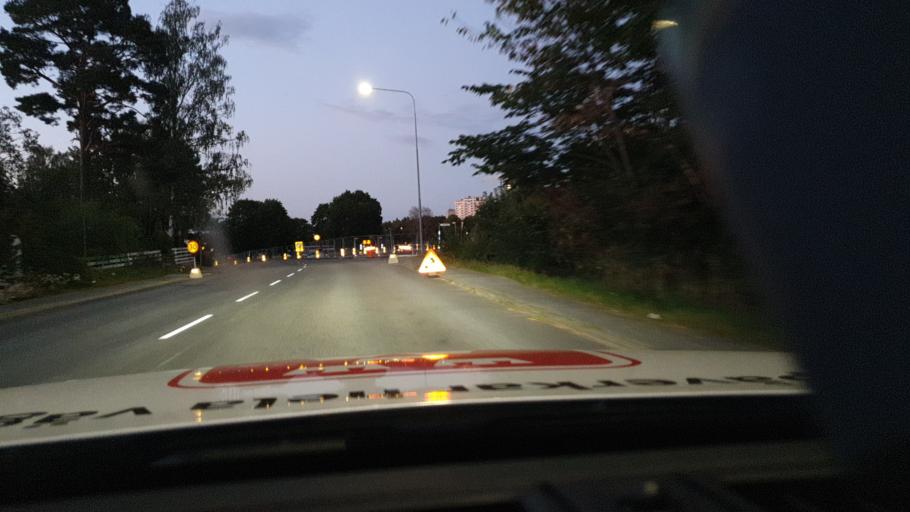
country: SE
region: Stockholm
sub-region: Taby Kommun
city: Taby
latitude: 59.4355
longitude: 18.0518
